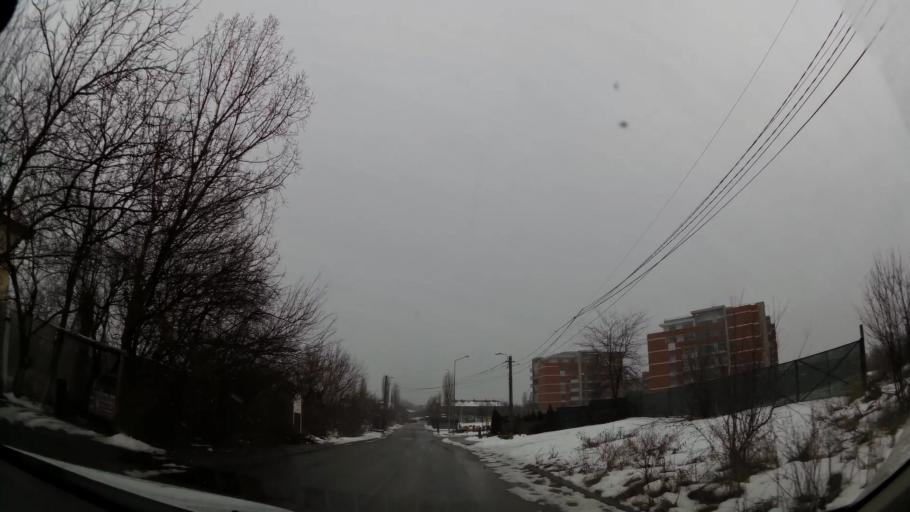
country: RO
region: Ilfov
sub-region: Comuna Otopeni
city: Otopeni
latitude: 44.5002
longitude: 26.0581
